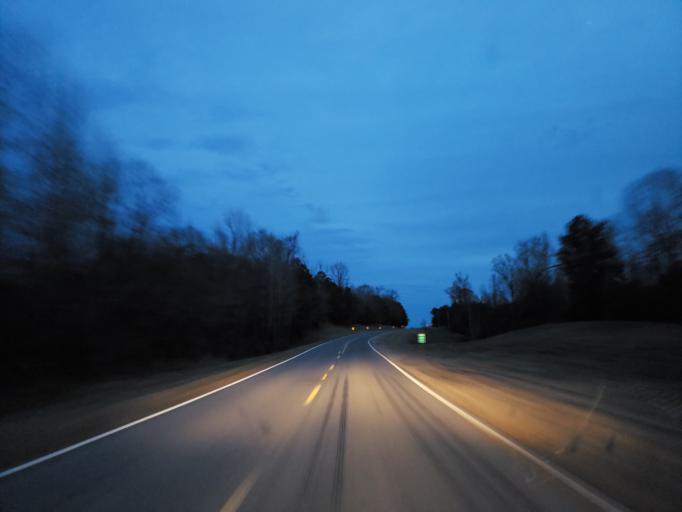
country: US
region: Alabama
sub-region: Greene County
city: Eutaw
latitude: 32.8937
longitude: -87.9537
